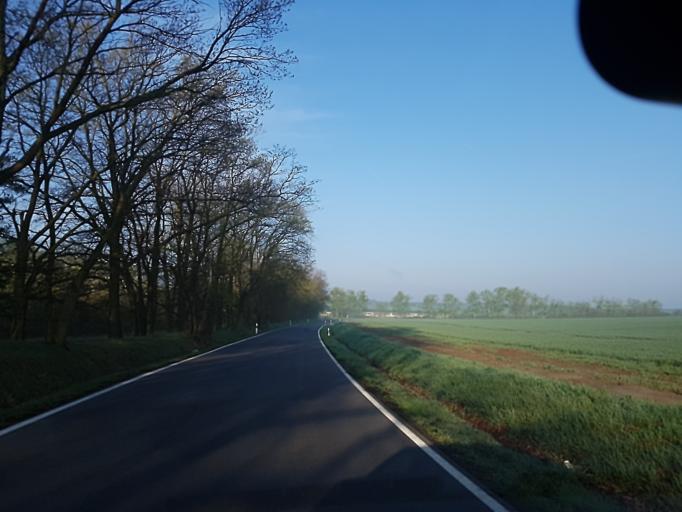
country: DE
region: Brandenburg
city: Muhlberg
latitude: 51.4379
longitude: 13.1656
